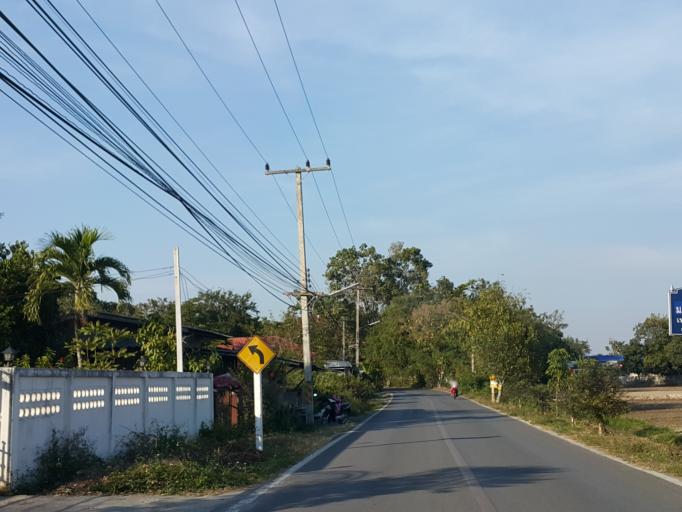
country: TH
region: Chiang Mai
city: San Sai
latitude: 18.7906
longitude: 99.0608
